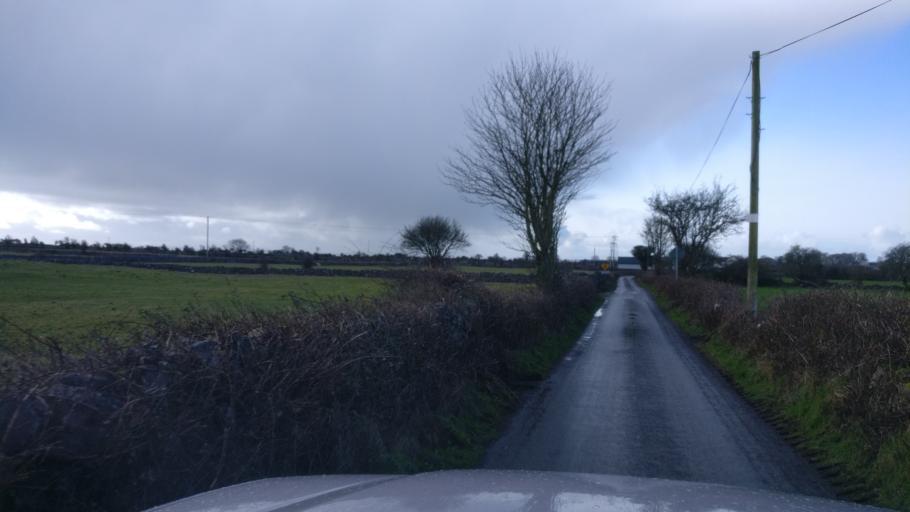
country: IE
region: Connaught
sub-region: County Galway
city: Oranmore
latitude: 53.2662
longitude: -8.8715
